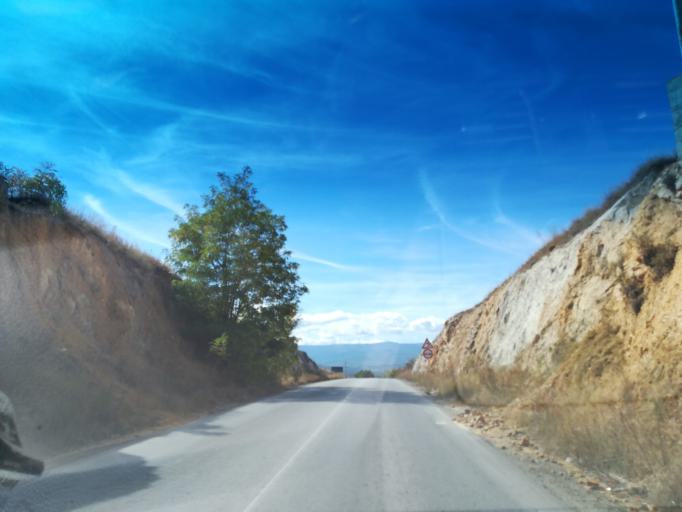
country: BG
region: Plovdiv
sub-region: Obshtina Krichim
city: Krichim
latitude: 42.0970
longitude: 24.4623
